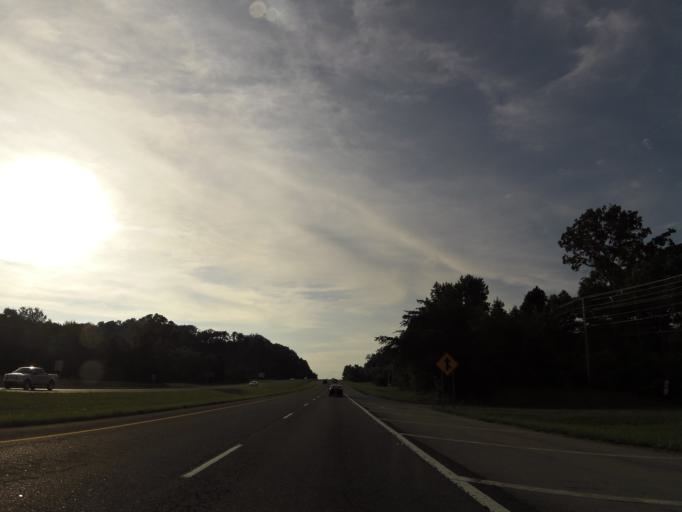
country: US
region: Tennessee
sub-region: Knox County
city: Farragut
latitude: 35.9361
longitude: -84.1461
